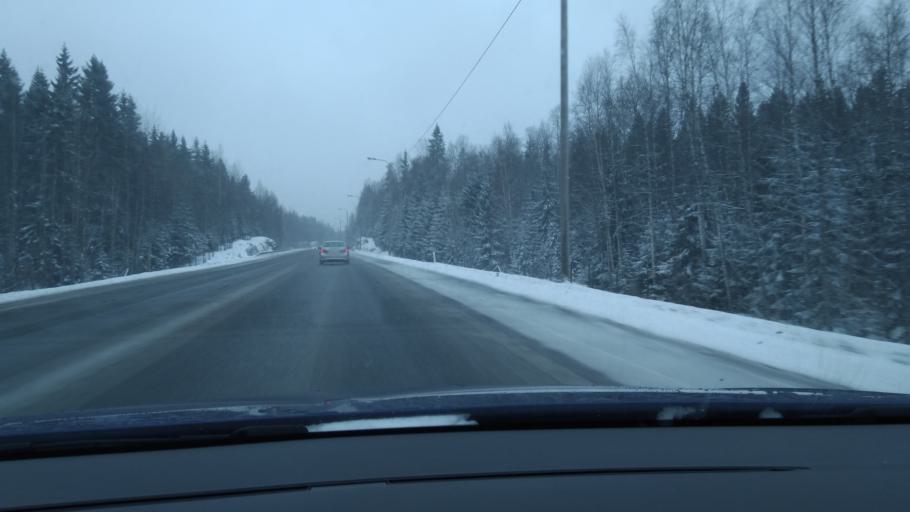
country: FI
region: Pirkanmaa
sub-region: Tampere
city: Tampere
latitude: 61.5155
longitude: 23.9154
